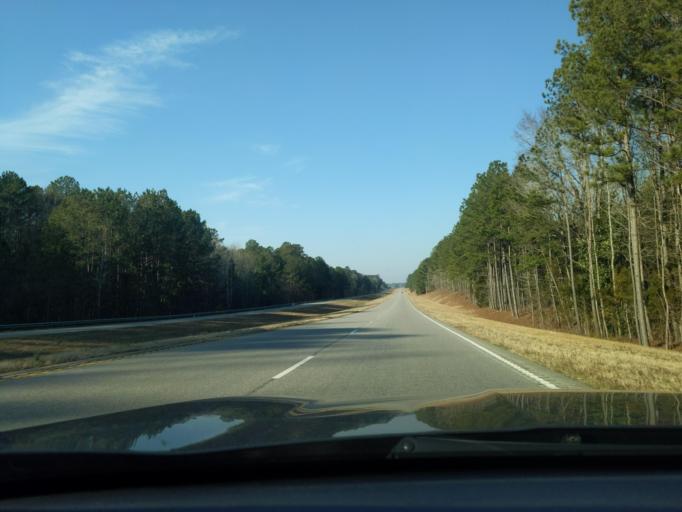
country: US
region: South Carolina
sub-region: Abbeville County
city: Abbeville
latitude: 34.1855
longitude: -82.2828
